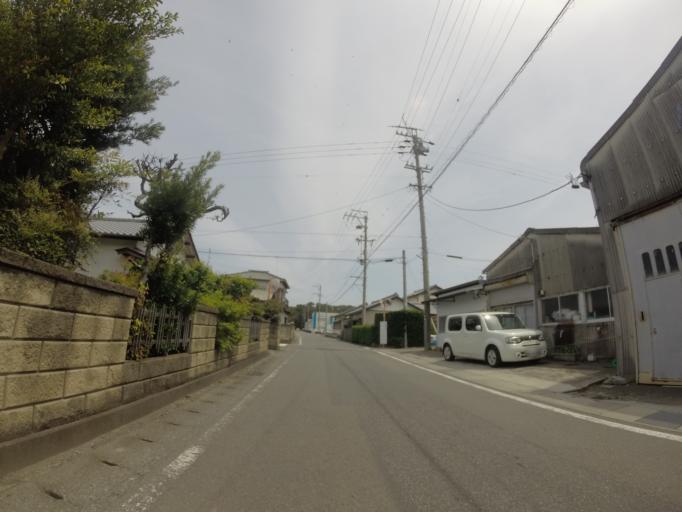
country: JP
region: Shizuoka
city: Yaizu
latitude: 34.8117
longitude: 138.3218
